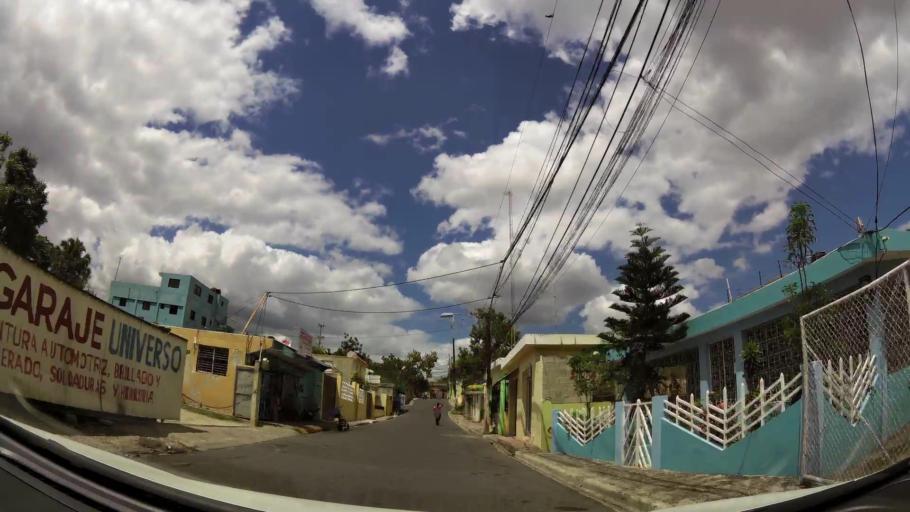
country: DO
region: Nacional
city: Ensanche Luperon
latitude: 18.5253
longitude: -69.9123
